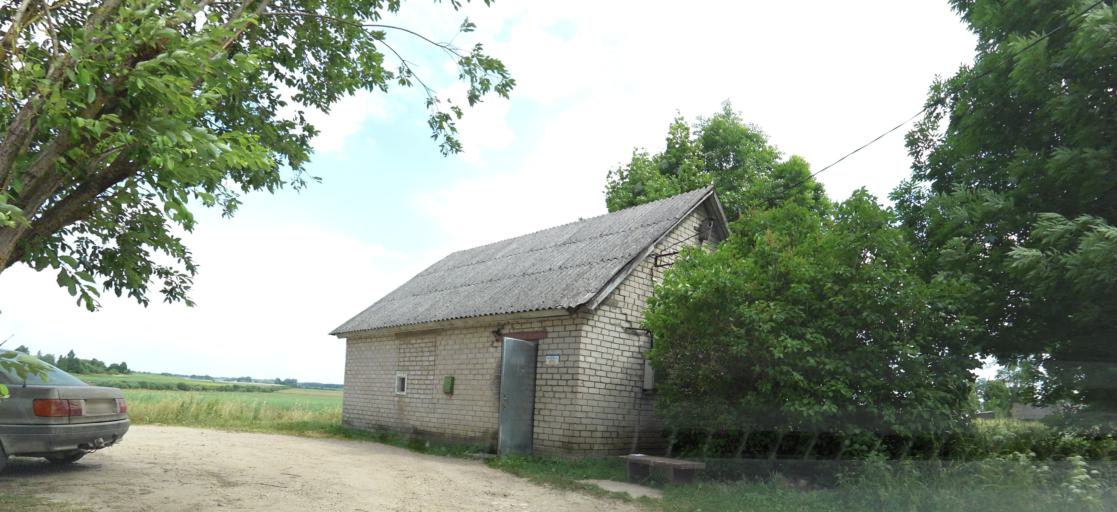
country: LT
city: Obeliai
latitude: 56.1470
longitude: 25.0449
